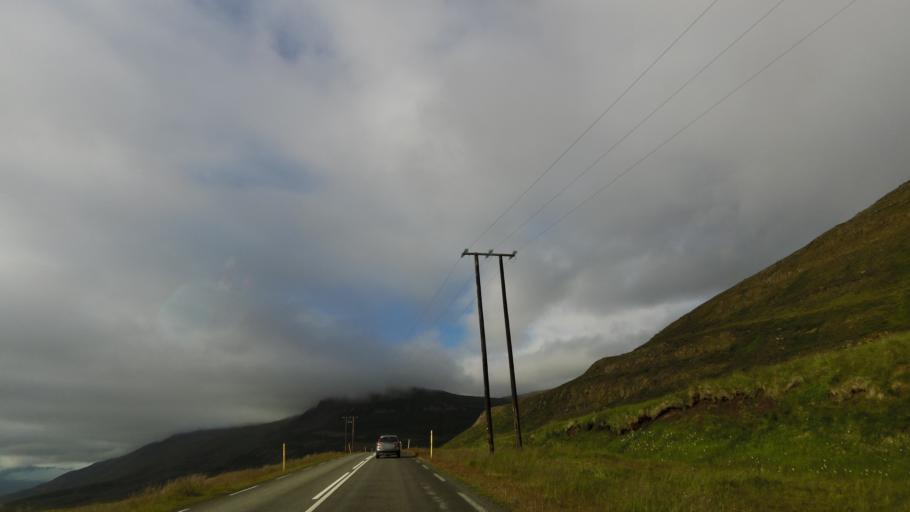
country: IS
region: Northeast
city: Akureyri
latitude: 65.8081
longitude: -18.0488
